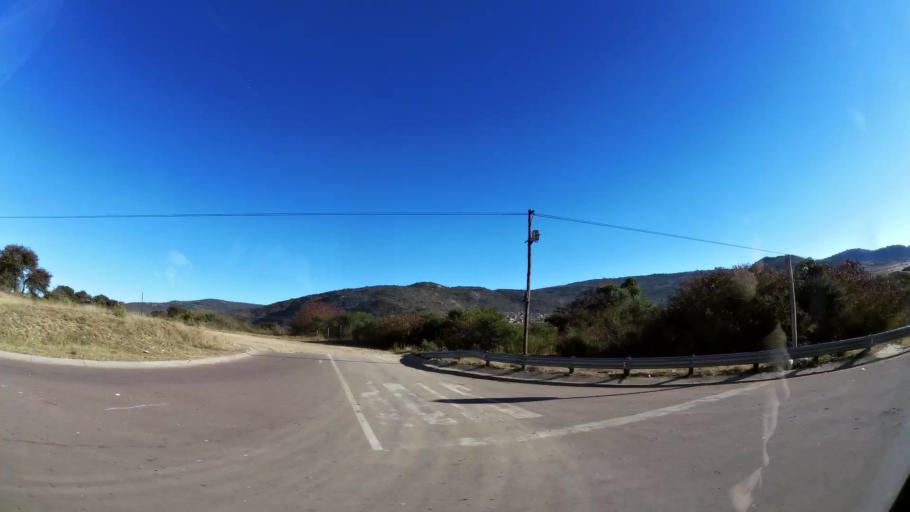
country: ZA
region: Limpopo
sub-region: Capricorn District Municipality
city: Mankoeng
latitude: -23.9233
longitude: 29.8769
